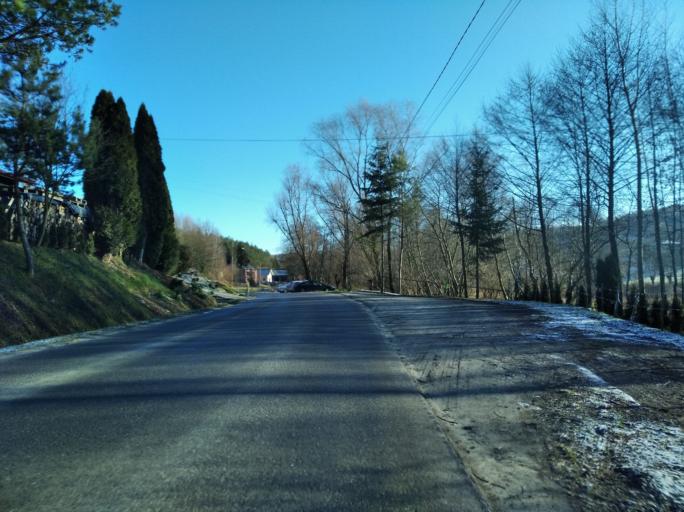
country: PL
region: Subcarpathian Voivodeship
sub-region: Powiat strzyzowski
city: Strzyzow
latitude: 49.9253
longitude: 21.7852
